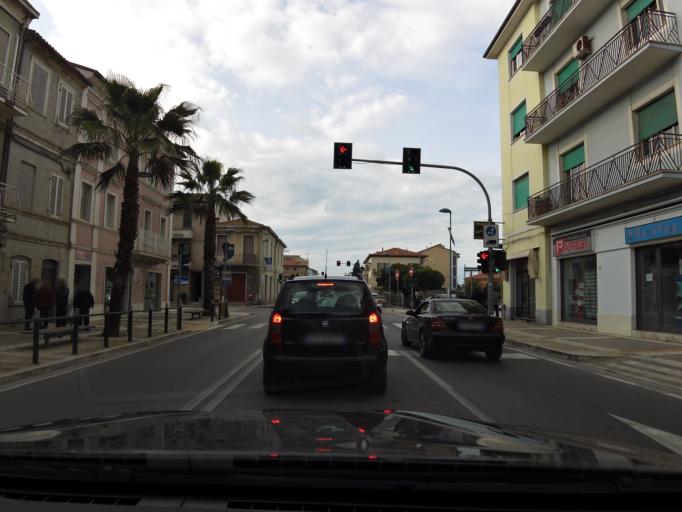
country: IT
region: The Marches
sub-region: Provincia di Macerata
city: Porto Potenza Picena
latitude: 43.3607
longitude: 13.6968
